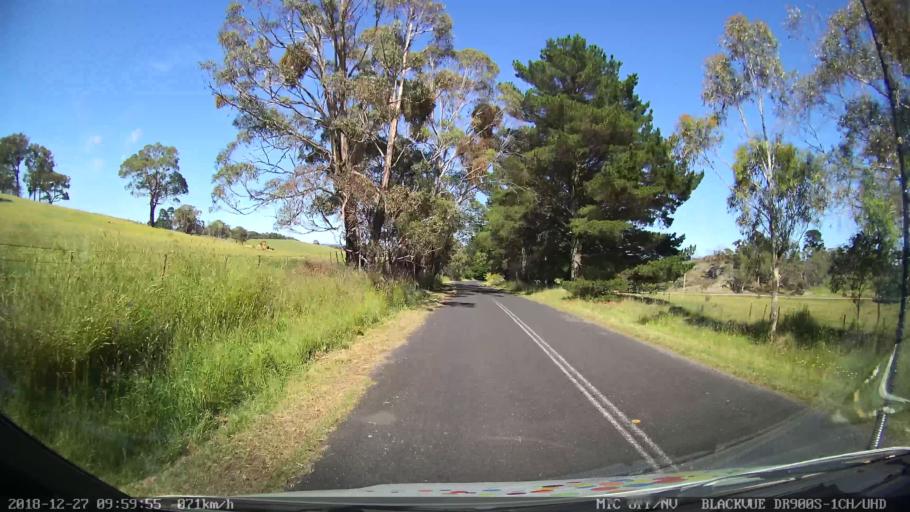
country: AU
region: New South Wales
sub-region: Lithgow
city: Portland
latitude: -33.4359
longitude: 149.9460
